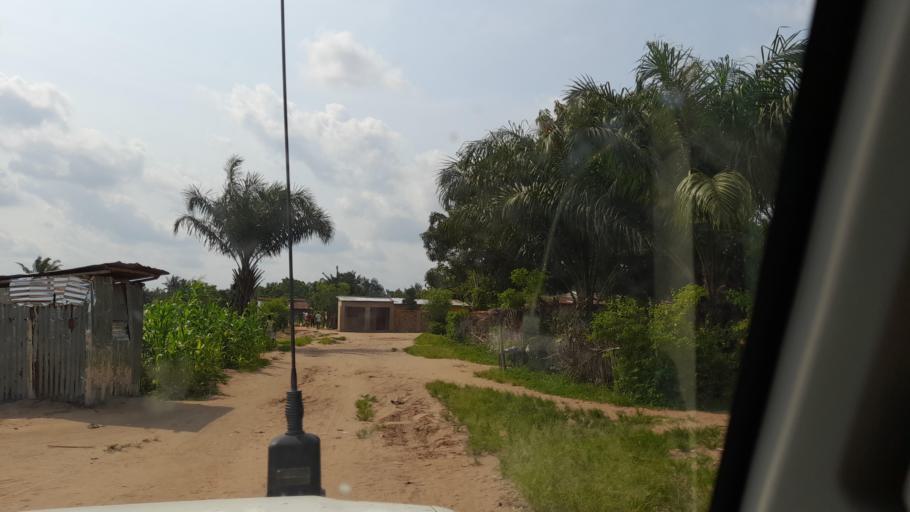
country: CD
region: Kasai-Occidental
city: Kananga
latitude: -5.9064
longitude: 22.4751
